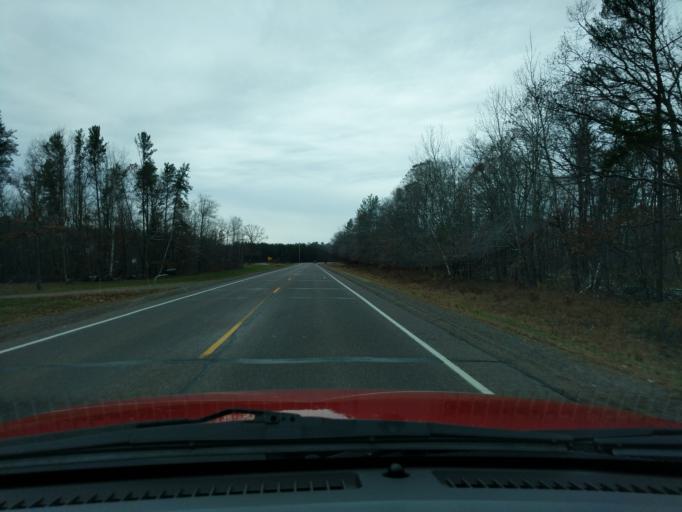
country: US
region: Wisconsin
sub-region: Washburn County
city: Spooner
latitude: 45.8171
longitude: -91.9642
